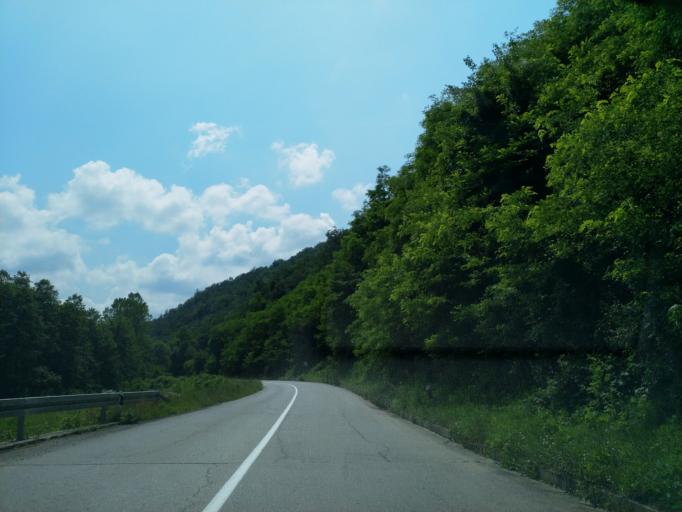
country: RS
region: Central Serbia
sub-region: Rasinski Okrug
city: Aleksandrovac
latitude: 43.3579
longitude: 20.9920
